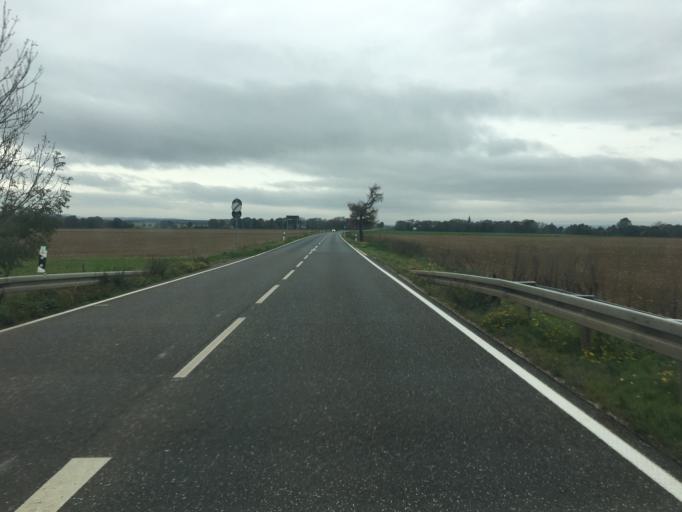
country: DE
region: North Rhine-Westphalia
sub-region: Regierungsbezirk Koln
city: Euskirchen
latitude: 50.6762
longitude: 6.7301
